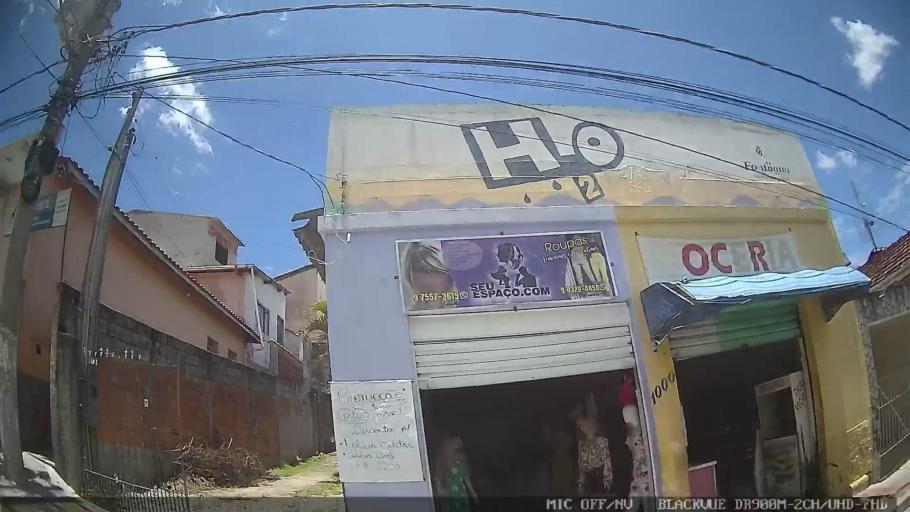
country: BR
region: Sao Paulo
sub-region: Santa Branca
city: Santa Branca
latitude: -23.5296
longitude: -45.8452
